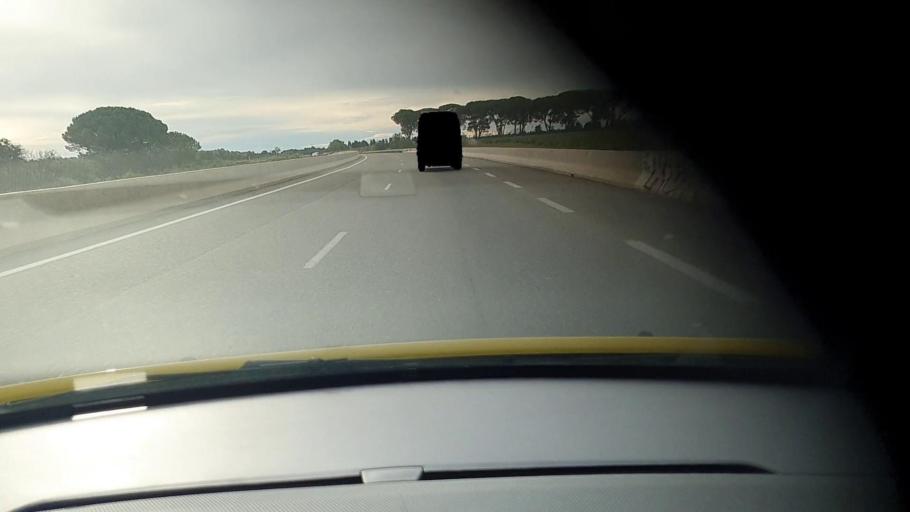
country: FR
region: Languedoc-Roussillon
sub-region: Departement du Gard
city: Caissargues
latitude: 43.7786
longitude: 4.3958
